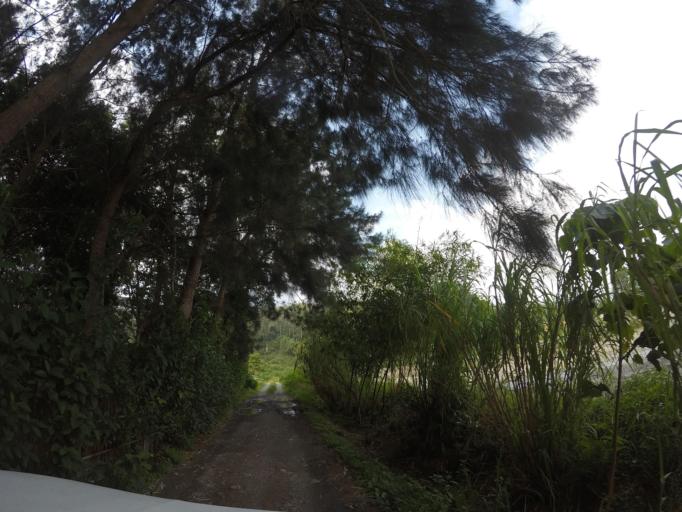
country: TL
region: Ermera
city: Gleno
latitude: -8.7129
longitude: 125.4398
